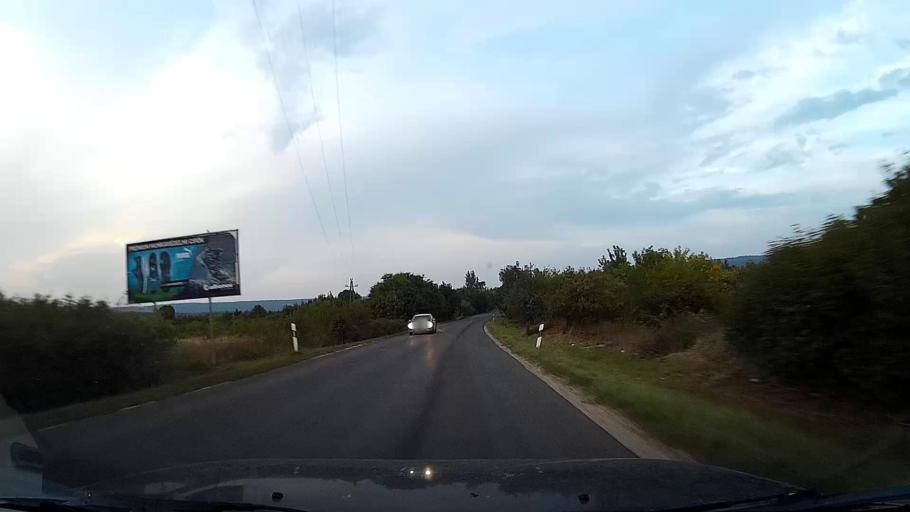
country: HU
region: Pest
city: Budakeszi
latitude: 47.4867
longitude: 18.9064
